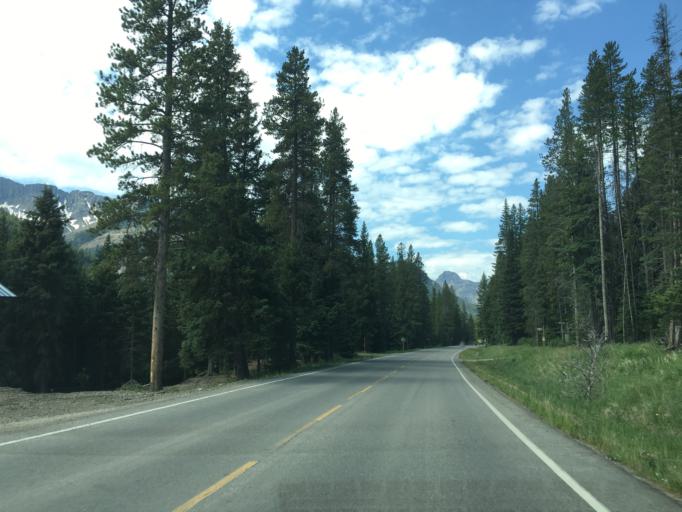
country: US
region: Montana
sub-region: Stillwater County
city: Absarokee
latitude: 45.0093
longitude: -109.9793
